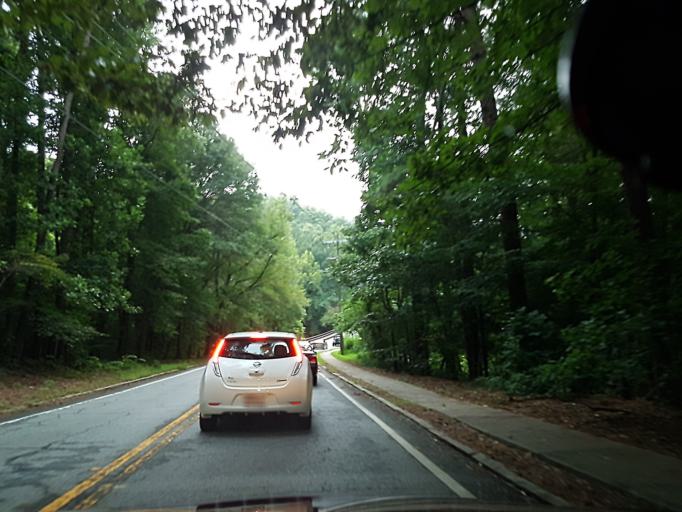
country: US
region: Georgia
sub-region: DeKalb County
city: North Druid Hills
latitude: 33.8052
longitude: -84.3221
